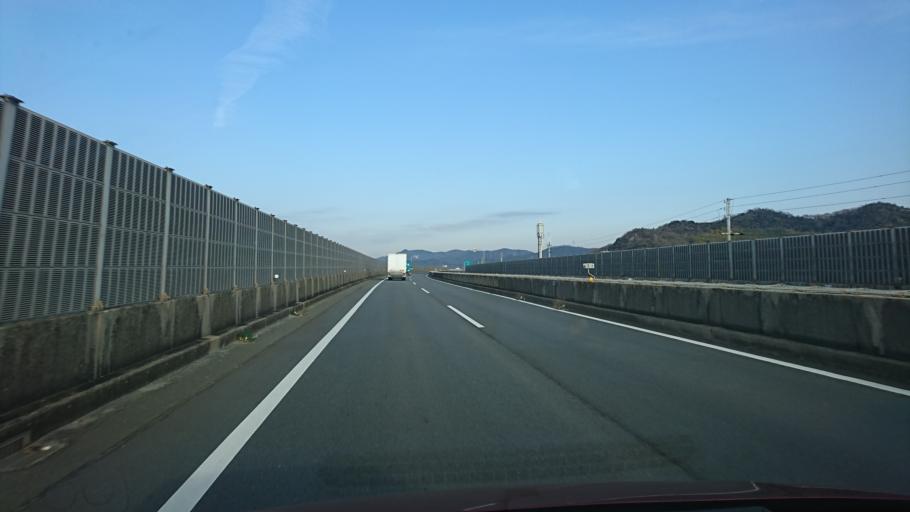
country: JP
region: Hyogo
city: Himeji
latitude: 34.8232
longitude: 134.7426
